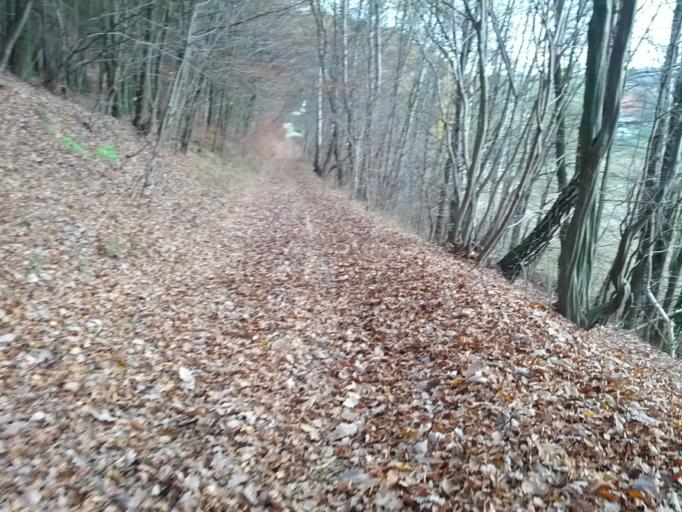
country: DE
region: Thuringia
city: Thal
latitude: 50.9400
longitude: 10.3474
